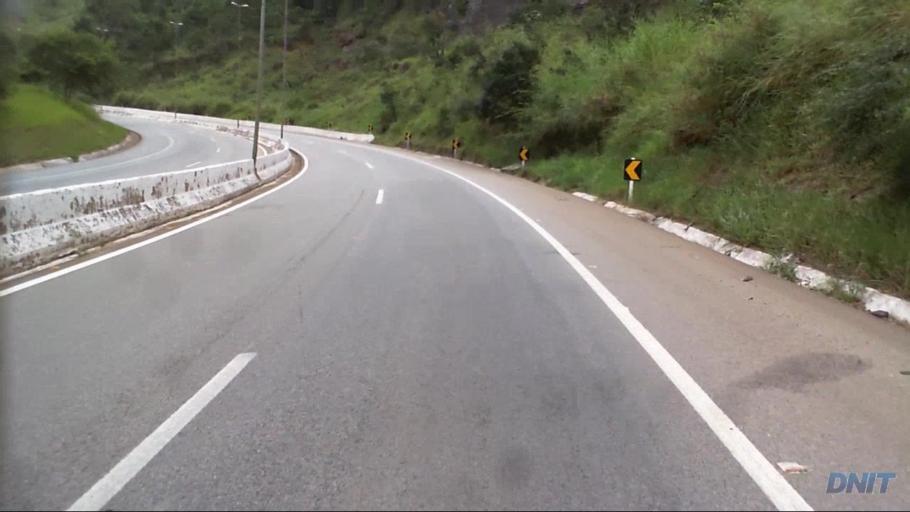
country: BR
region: Minas Gerais
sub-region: Nova Era
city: Nova Era
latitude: -19.7600
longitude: -43.0337
